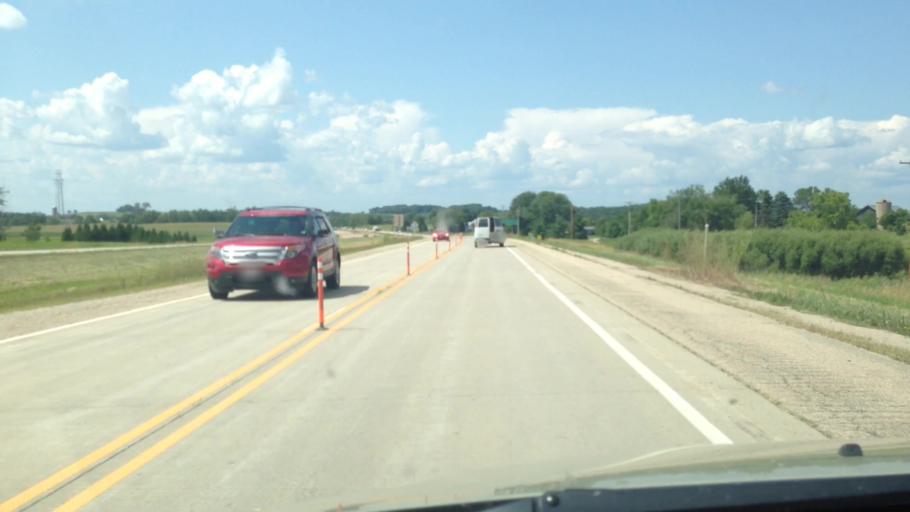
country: US
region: Wisconsin
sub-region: Shawano County
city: Bonduel
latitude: 44.7096
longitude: -88.3805
